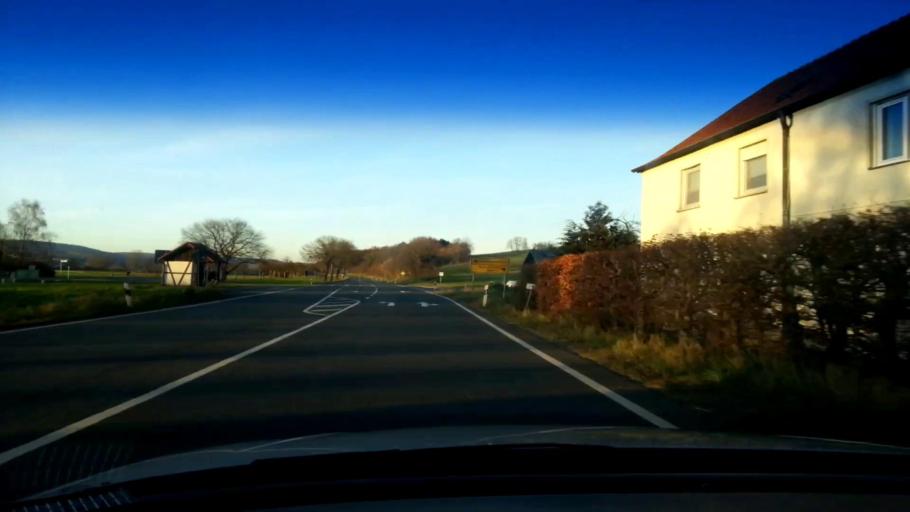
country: DE
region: Bavaria
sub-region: Upper Franconia
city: Rattelsdorf
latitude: 50.0471
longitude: 10.8824
